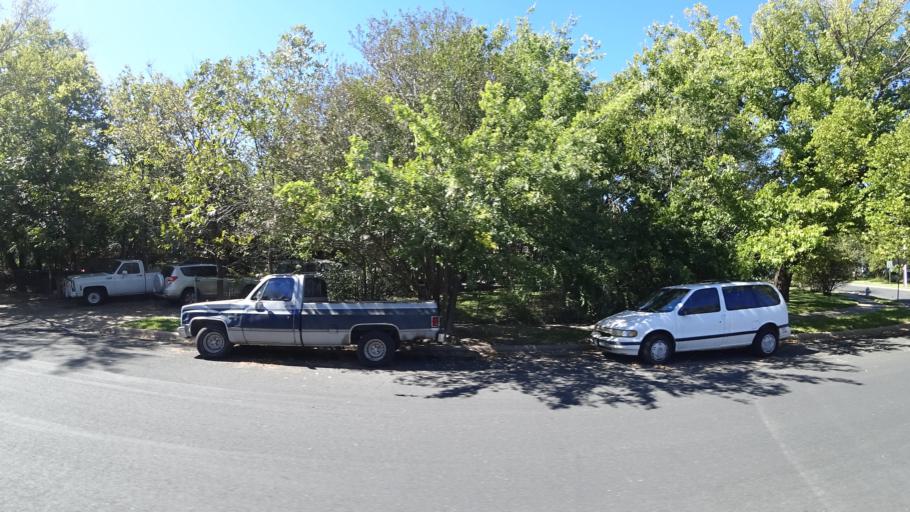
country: US
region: Texas
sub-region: Travis County
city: Austin
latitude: 30.3349
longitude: -97.7258
